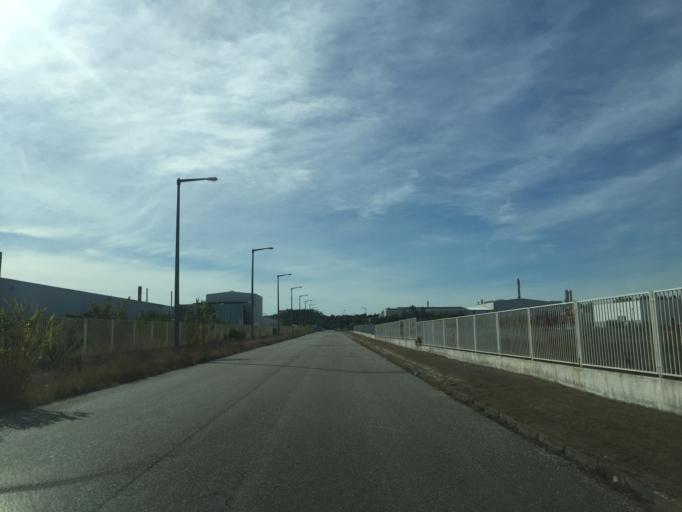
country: PT
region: Coimbra
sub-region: Figueira da Foz
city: Lavos
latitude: 40.1099
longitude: -8.8474
